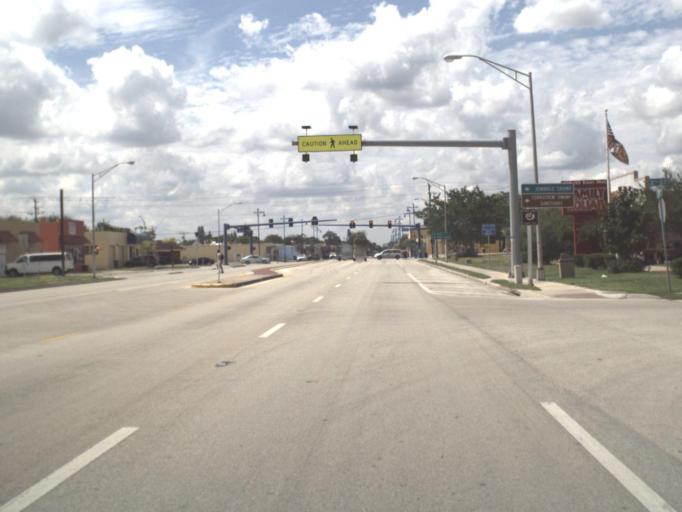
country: US
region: Florida
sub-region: Collier County
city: Immokalee
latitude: 26.4187
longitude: -81.4158
